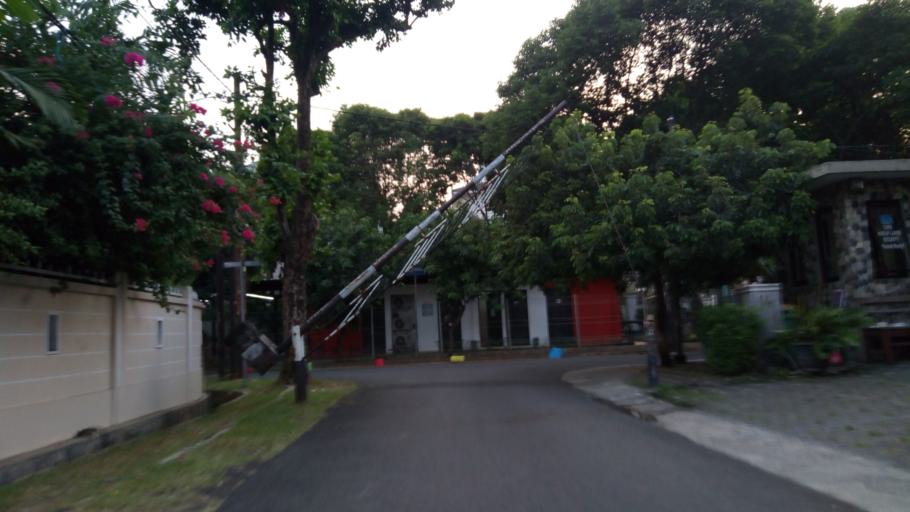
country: ID
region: Jakarta Raya
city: Jakarta
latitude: -6.2432
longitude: 106.7901
